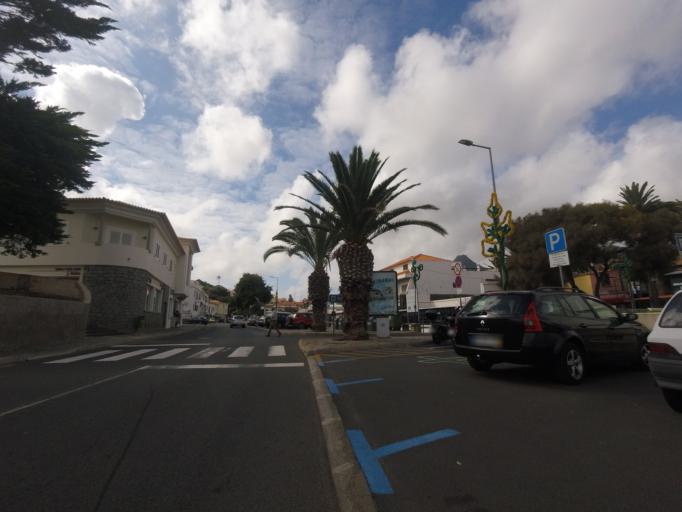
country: PT
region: Madeira
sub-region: Porto Santo
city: Vila de Porto Santo
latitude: 33.0595
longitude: -16.3338
